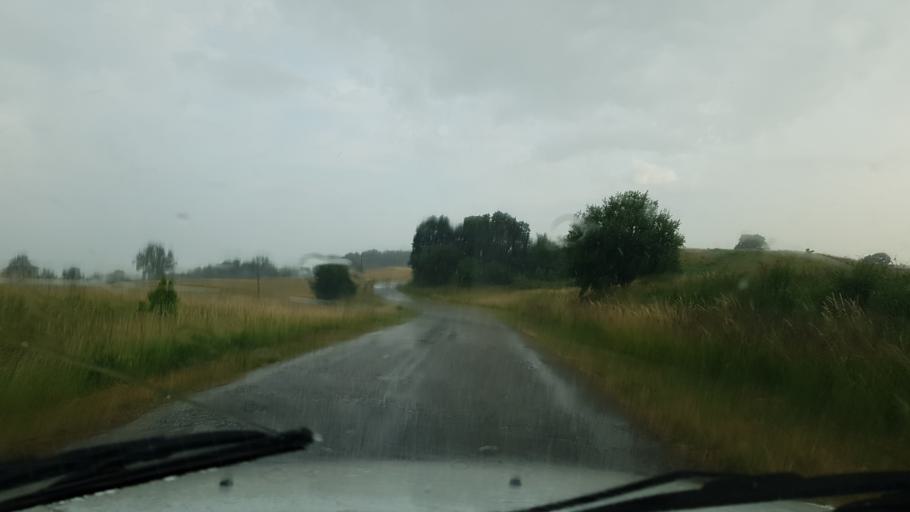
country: PL
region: West Pomeranian Voivodeship
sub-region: Powiat lobeski
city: Lobez
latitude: 53.6486
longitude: 15.6737
